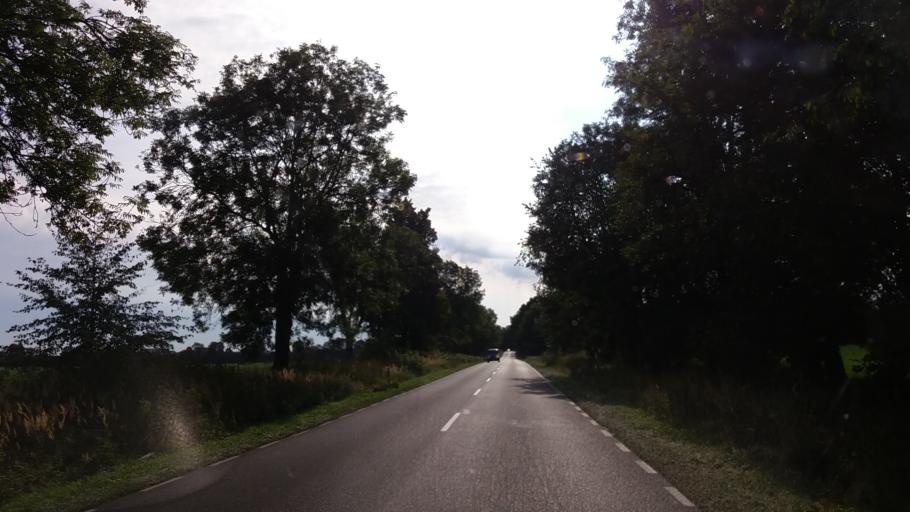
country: PL
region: West Pomeranian Voivodeship
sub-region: Powiat stargardzki
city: Suchan
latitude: 53.2133
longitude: 15.3134
